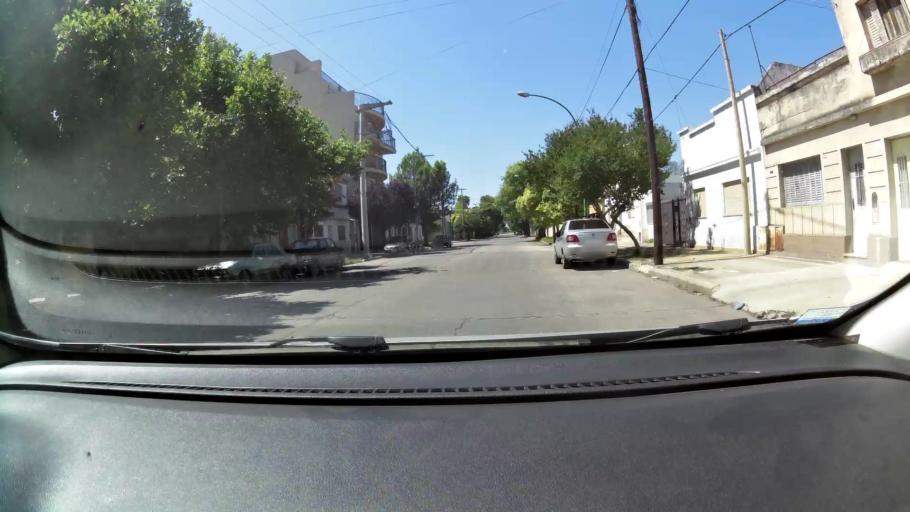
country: AR
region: Cordoba
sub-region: Departamento de Capital
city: Cordoba
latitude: -31.3944
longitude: -64.1925
